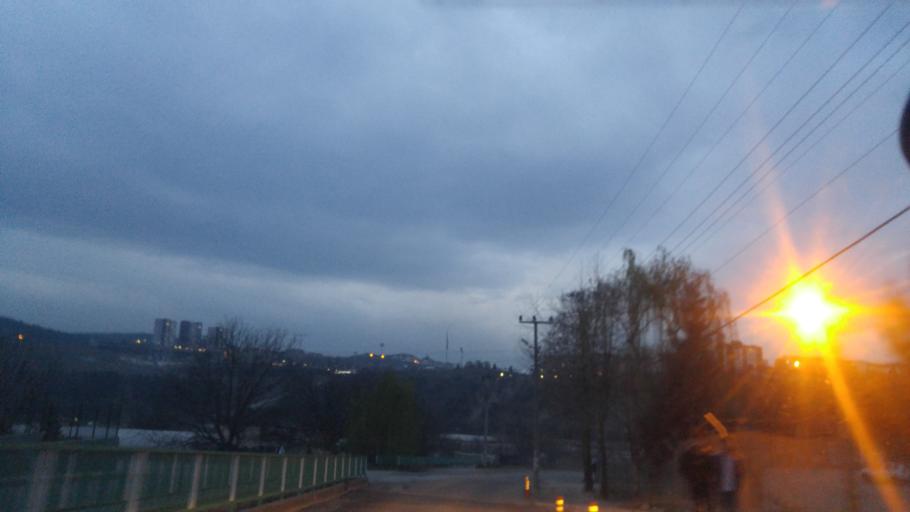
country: TR
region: Karabuk
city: Karabuk
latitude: 41.2150
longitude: 32.6603
